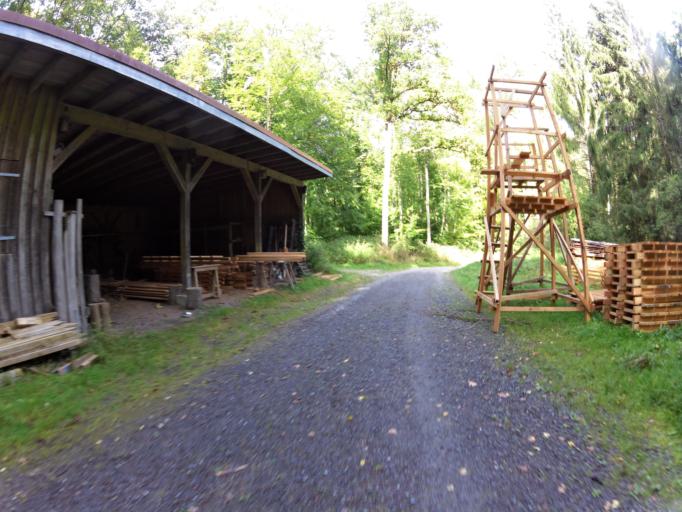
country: DE
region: Bavaria
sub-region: Regierungsbezirk Unterfranken
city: Waldbrunn
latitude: 49.7281
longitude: 9.8145
